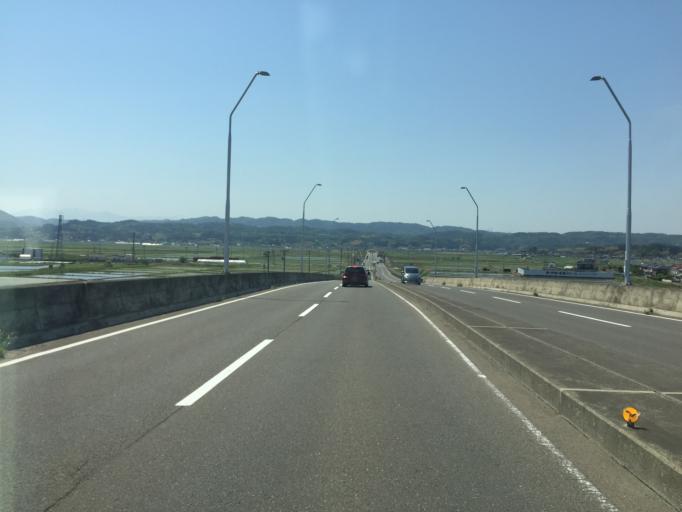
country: JP
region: Miyagi
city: Iwanuma
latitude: 38.1400
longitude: 140.8787
